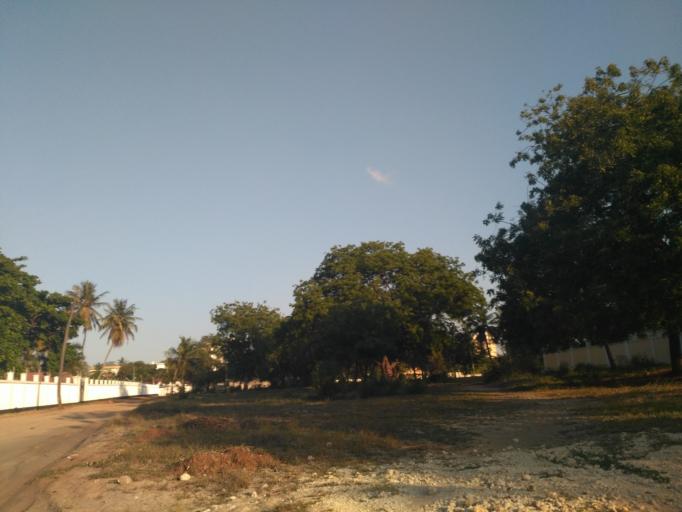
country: TZ
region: Dar es Salaam
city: Magomeni
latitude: -6.7588
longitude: 39.2525
